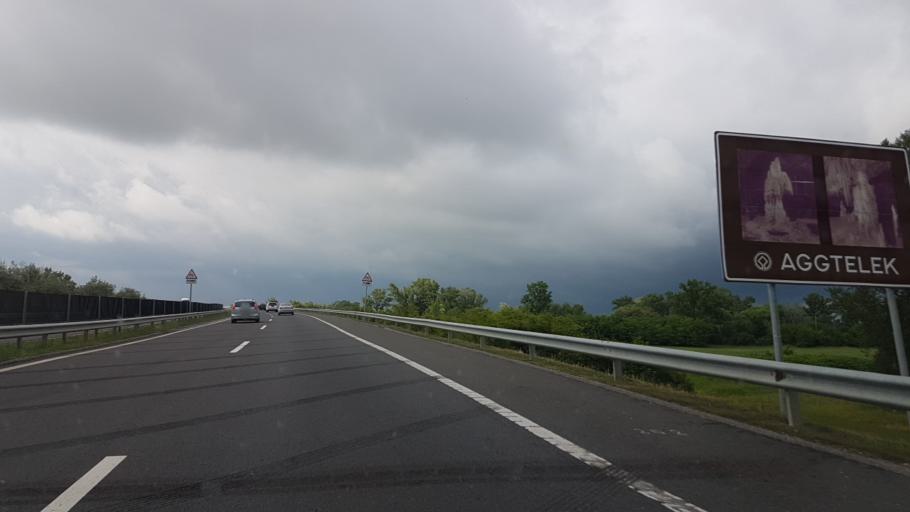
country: HU
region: Borsod-Abauj-Zemplen
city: Felsozsolca
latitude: 48.0848
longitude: 20.8512
